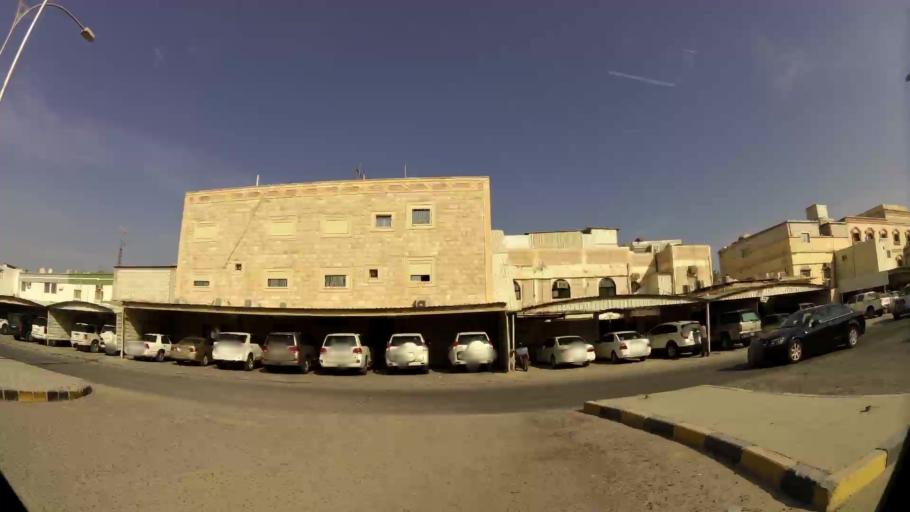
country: KW
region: Al Ahmadi
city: Ar Riqqah
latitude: 29.1456
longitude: 48.1066
